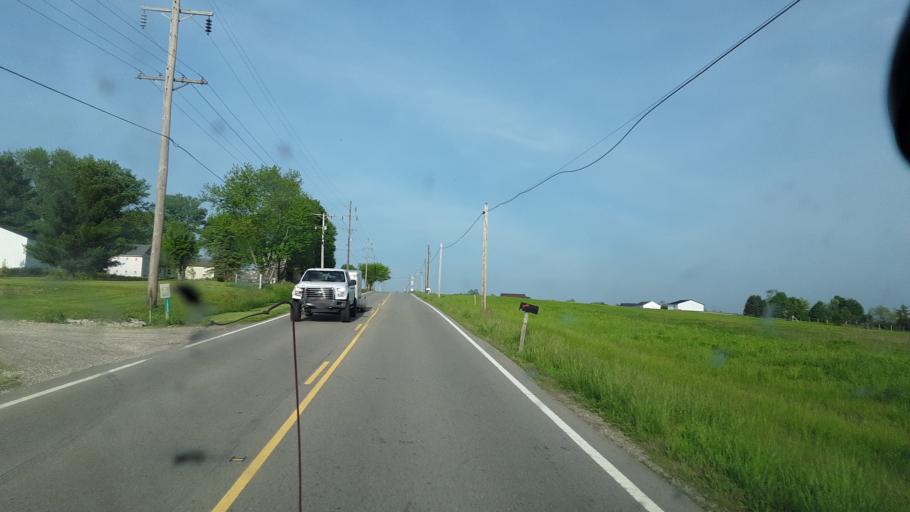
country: US
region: Ohio
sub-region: Ross County
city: Kingston
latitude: 39.5141
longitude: -82.7904
